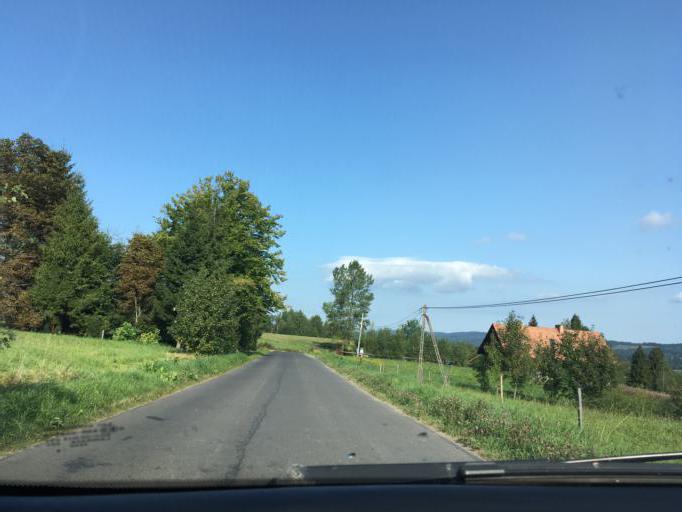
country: PL
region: Subcarpathian Voivodeship
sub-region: Powiat bieszczadzki
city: Czarna
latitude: 49.3143
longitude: 22.6825
